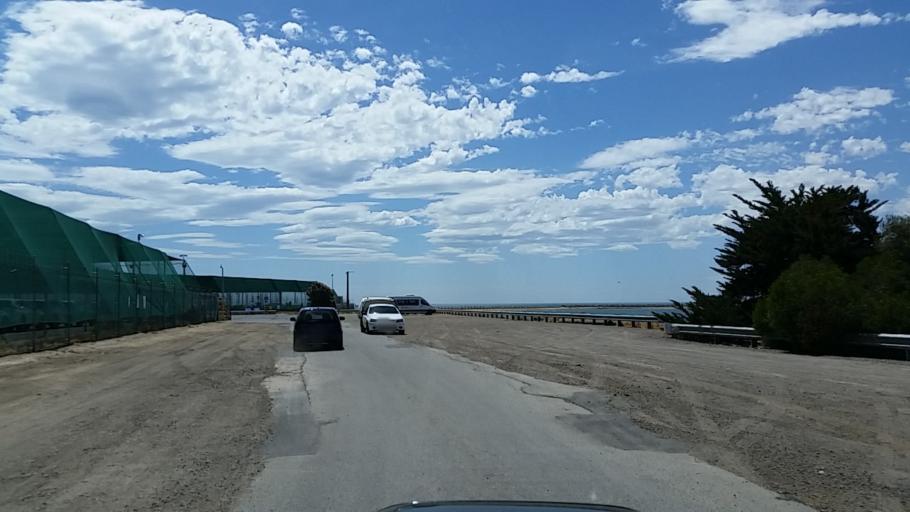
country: AU
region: South Australia
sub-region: Port Adelaide Enfield
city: Birkenhead
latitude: -34.7751
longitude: 138.4874
